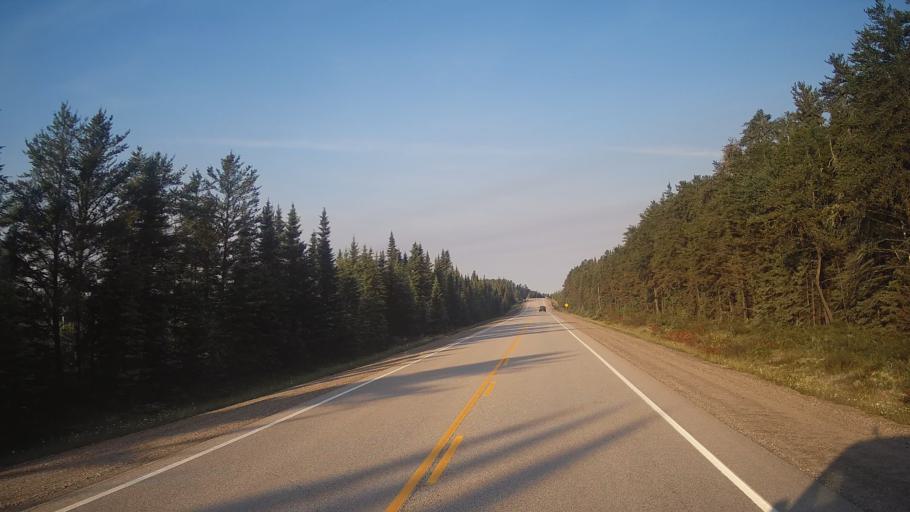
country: CA
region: Ontario
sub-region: Rainy River District
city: Atikokan
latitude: 49.2477
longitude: -91.0672
